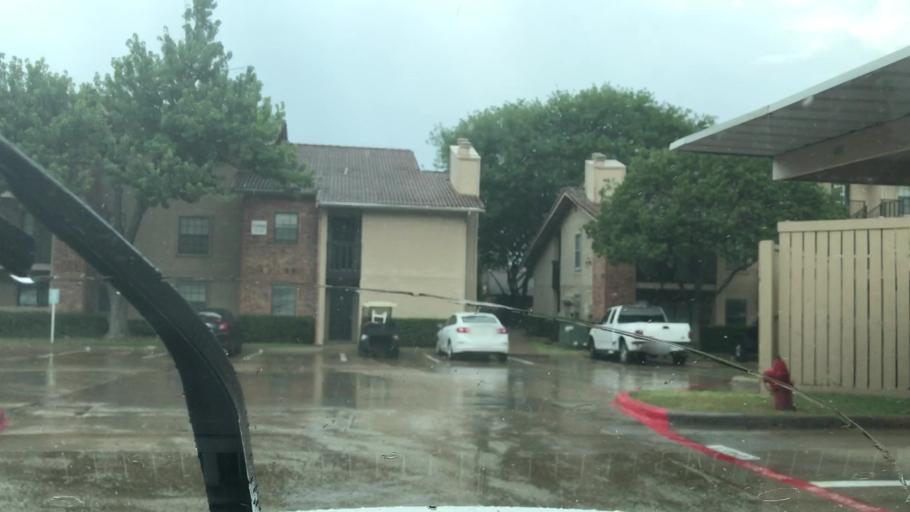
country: US
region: Texas
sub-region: Dallas County
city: Farmers Branch
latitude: 32.9047
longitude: -96.9622
